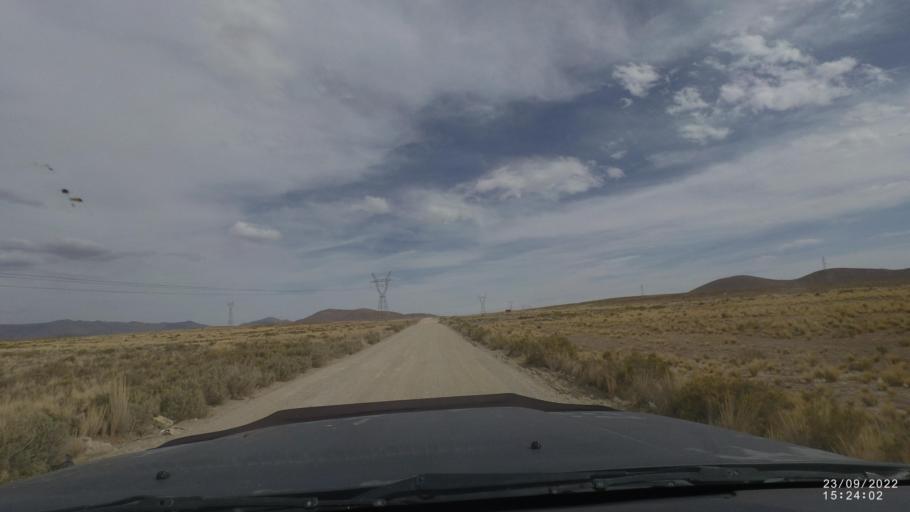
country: BO
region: Oruro
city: Oruro
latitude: -17.9318
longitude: -67.0408
